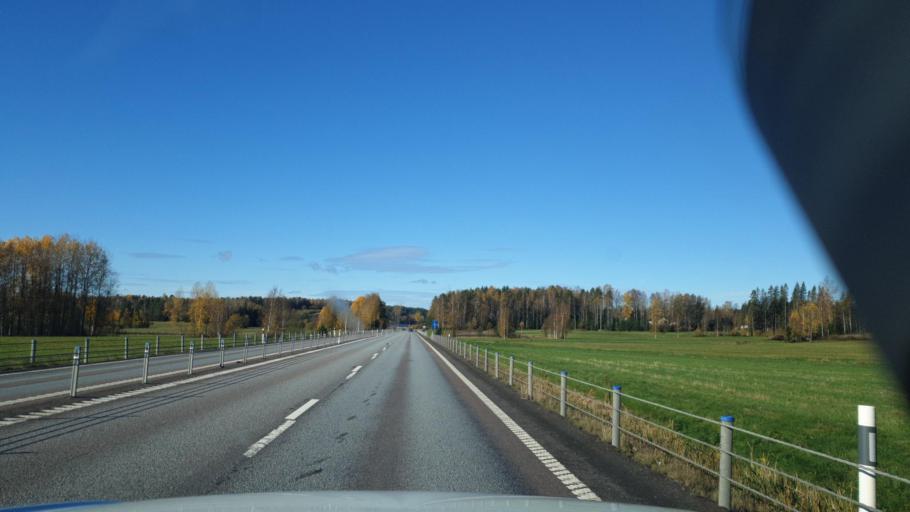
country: SE
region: Vaermland
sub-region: Arvika Kommun
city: Arvika
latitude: 59.6529
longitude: 12.6653
